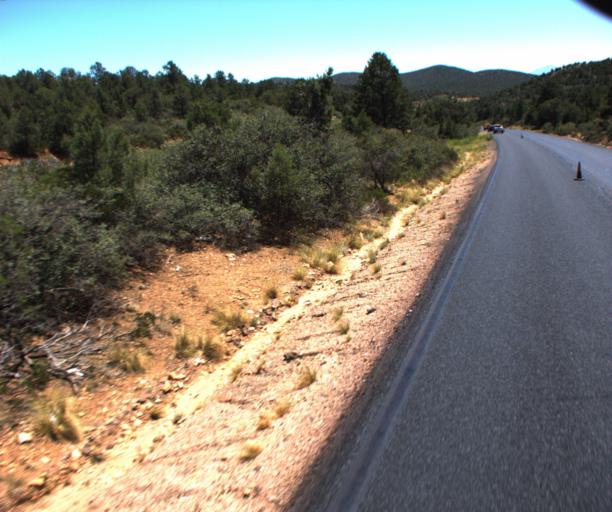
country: US
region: Arizona
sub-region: Gila County
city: Payson
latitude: 34.2035
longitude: -111.3314
